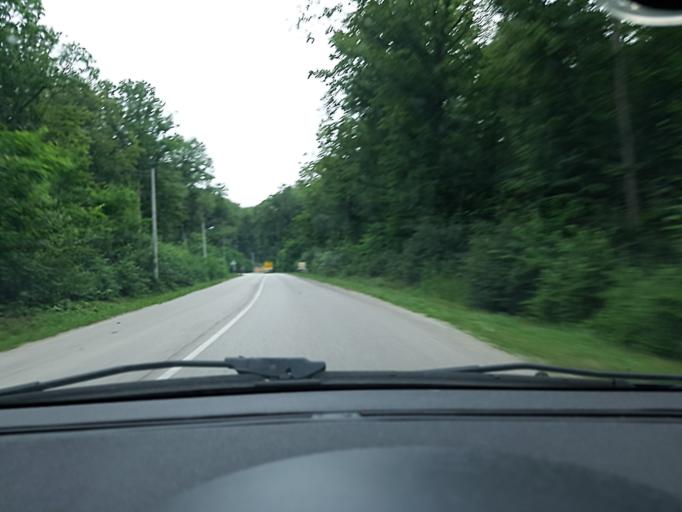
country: HR
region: Zagrebacka
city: Pojatno
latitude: 45.8891
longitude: 15.7943
